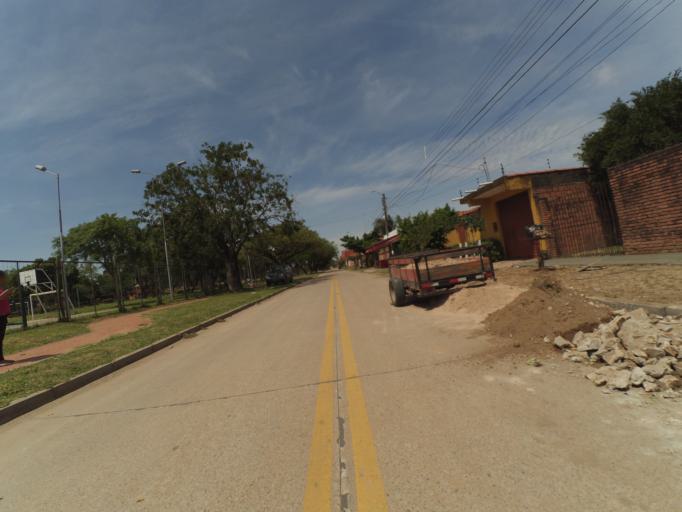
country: BO
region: Santa Cruz
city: Santa Cruz de la Sierra
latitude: -17.8321
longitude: -63.2360
